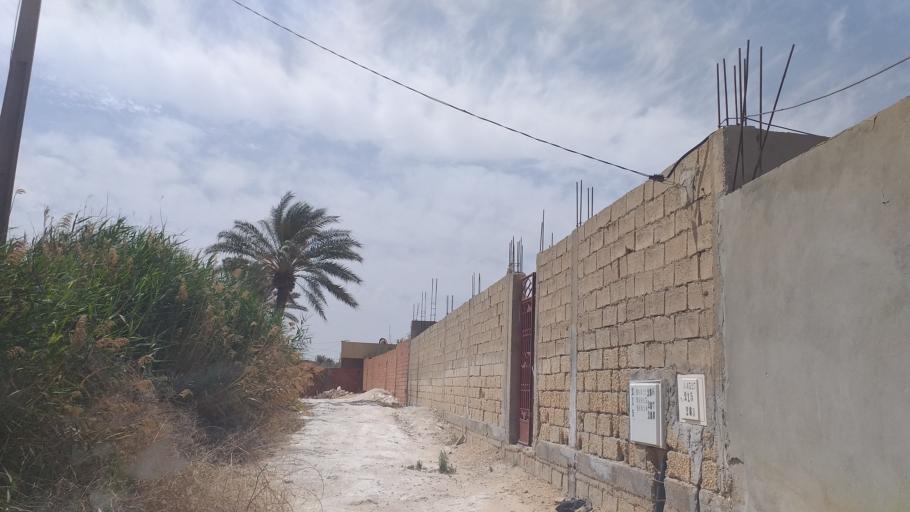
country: TN
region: Qabis
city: Gabes
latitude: 33.9482
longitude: 10.0651
